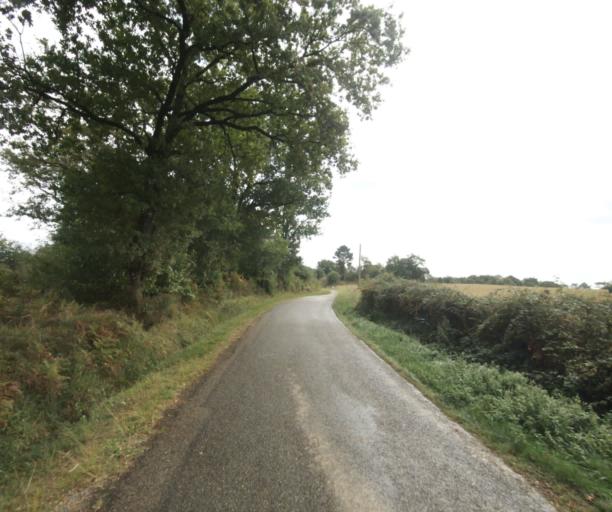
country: FR
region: Midi-Pyrenees
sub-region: Departement du Gers
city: Cazaubon
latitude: 43.8959
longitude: -0.1231
